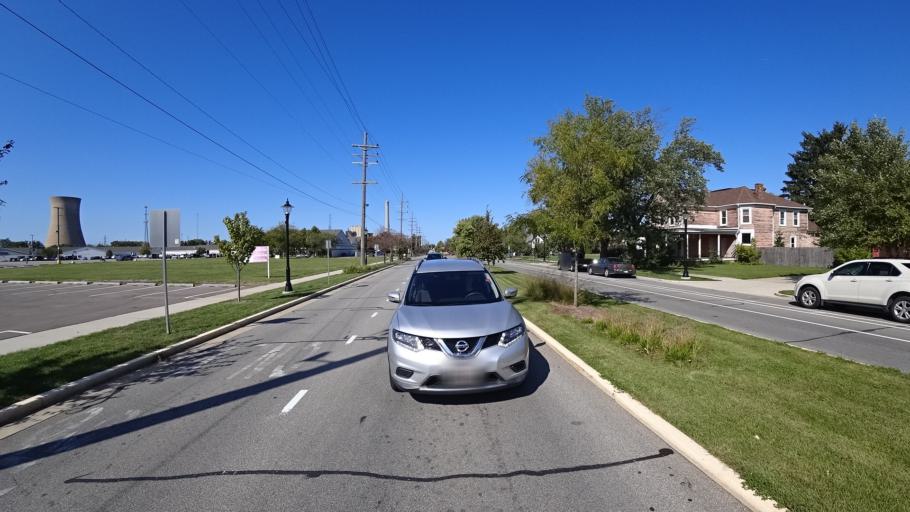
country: US
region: Indiana
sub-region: LaPorte County
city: Michigan City
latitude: 41.7133
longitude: -86.9033
